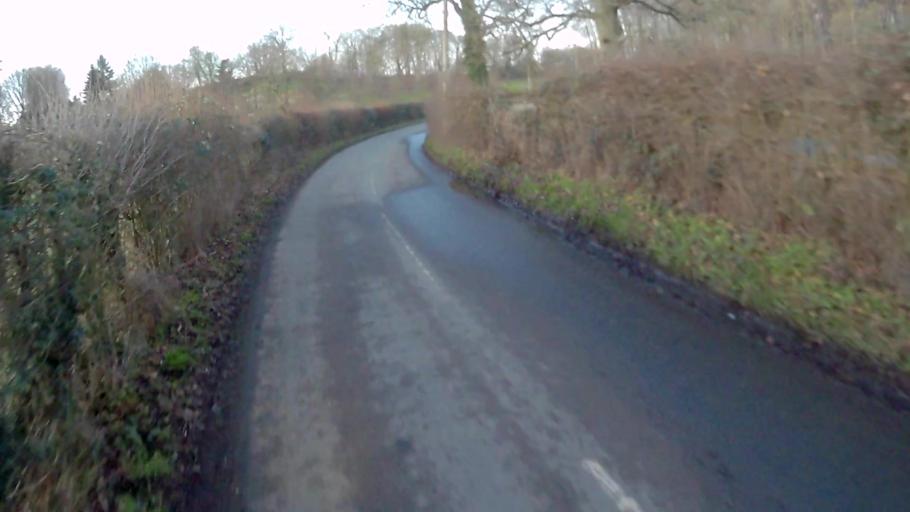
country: GB
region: England
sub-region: Hampshire
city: Overton
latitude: 51.2368
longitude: -1.2208
